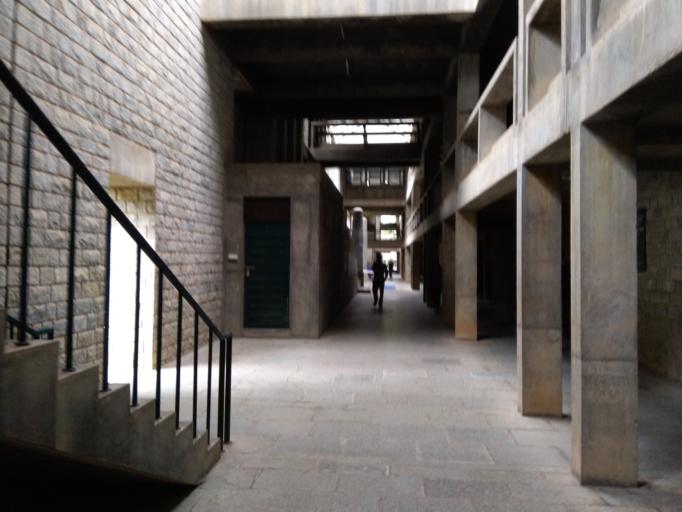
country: IN
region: Karnataka
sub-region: Bangalore Urban
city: Bangalore
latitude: 12.8941
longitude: 77.6010
